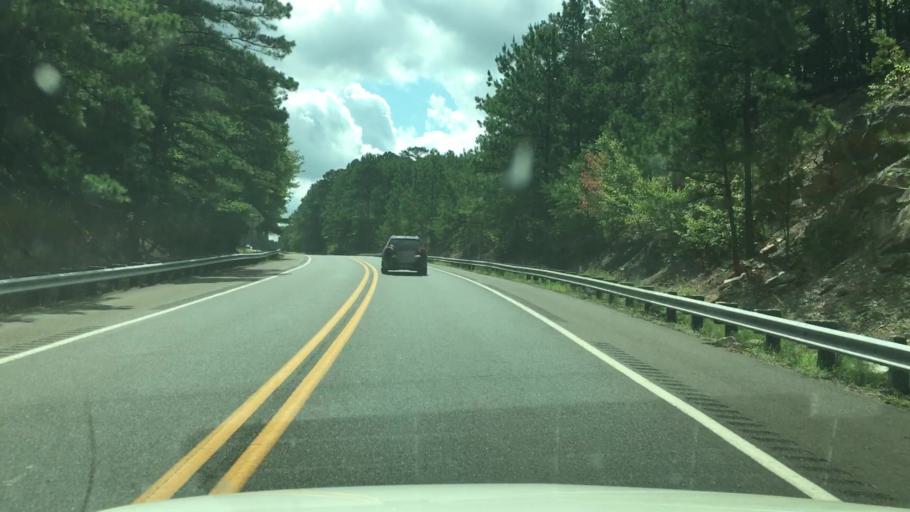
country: US
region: Arkansas
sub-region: Clark County
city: Arkadelphia
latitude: 34.2309
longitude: -93.0978
